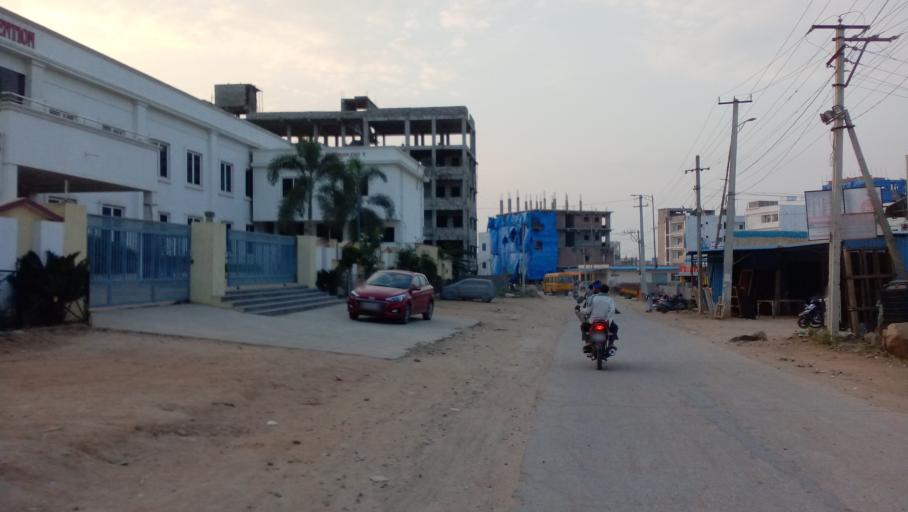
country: IN
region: Telangana
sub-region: Medak
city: Serilingampalle
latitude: 17.5218
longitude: 78.3022
